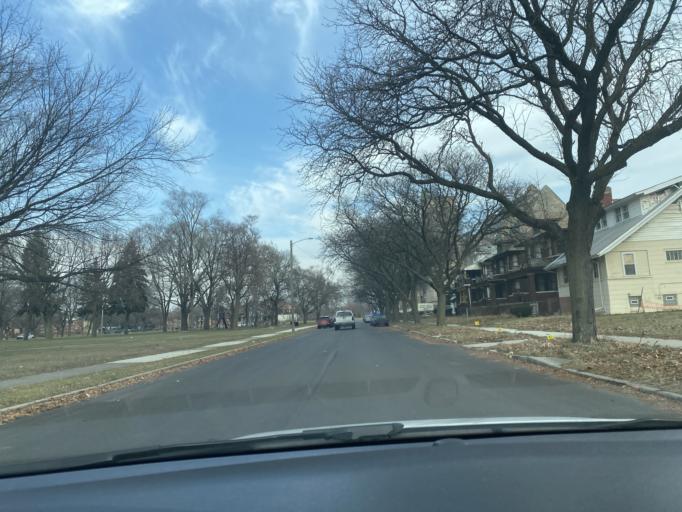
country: US
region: Michigan
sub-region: Wayne County
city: Highland Park
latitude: 42.3667
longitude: -83.1326
